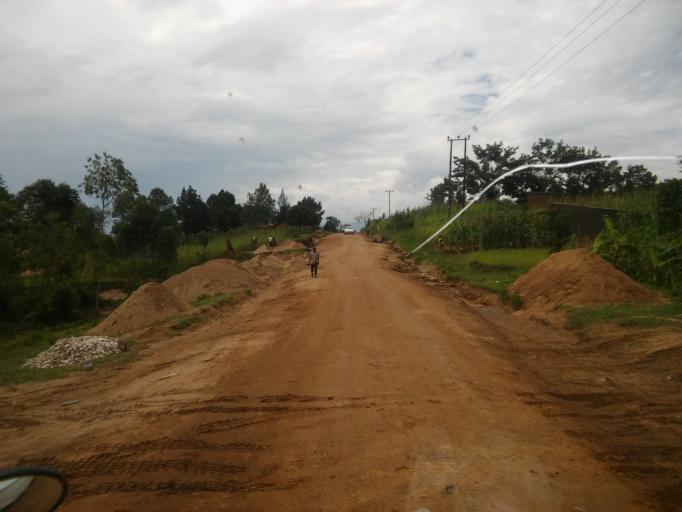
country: KE
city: Malikisi
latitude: 0.8146
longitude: 34.3443
